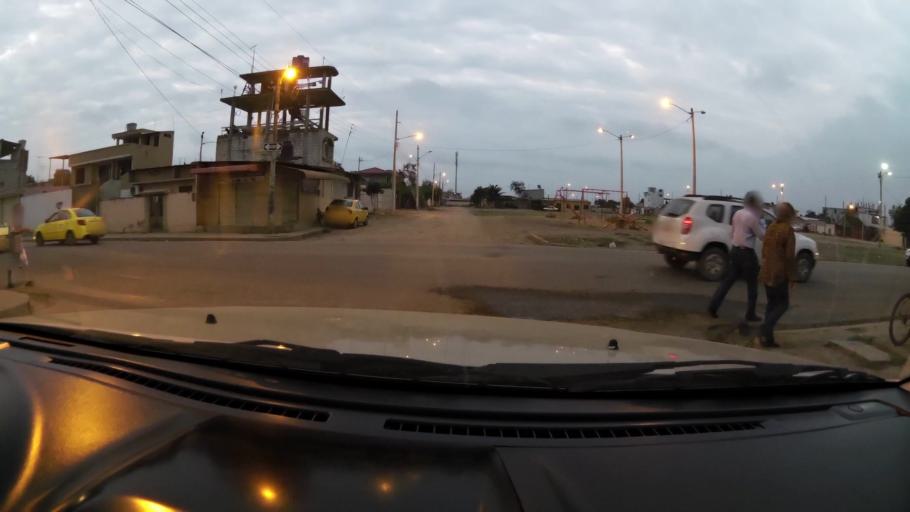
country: EC
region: El Oro
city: Machala
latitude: -3.2638
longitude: -79.9362
